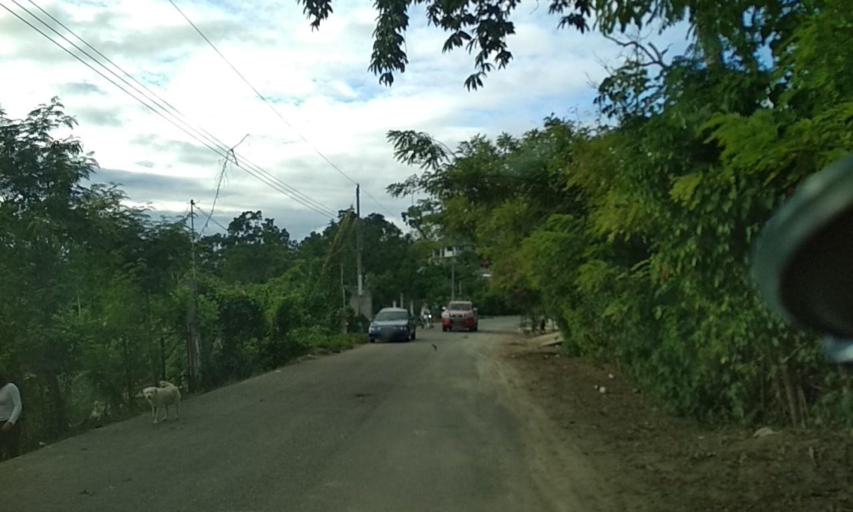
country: MX
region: Veracruz
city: Cazones de Herrera
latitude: 20.6407
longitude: -97.3385
